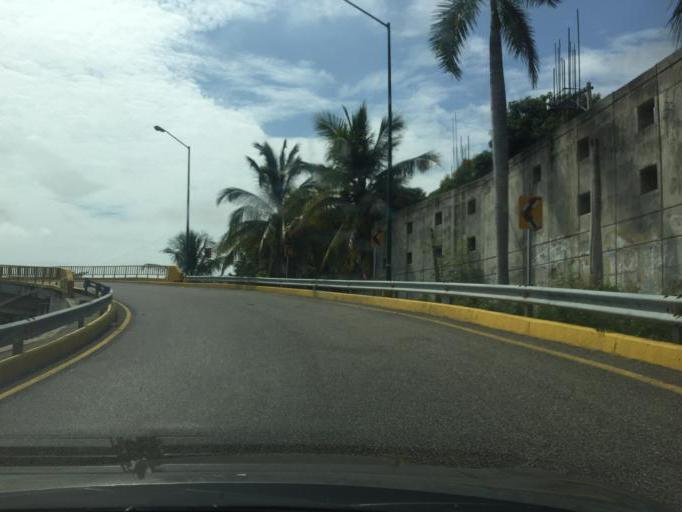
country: MX
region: Guerrero
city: Acapulco de Juarez
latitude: 16.8718
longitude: -99.8699
